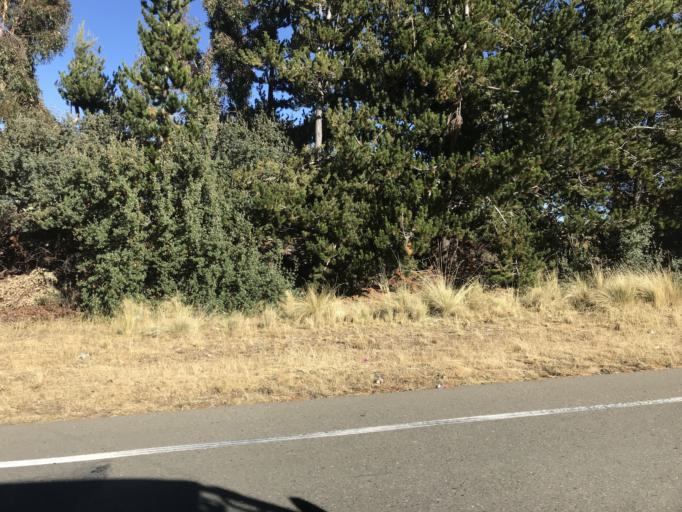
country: PE
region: Puno
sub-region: Yunguyo
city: Yunguyo
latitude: -16.1733
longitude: -68.9826
